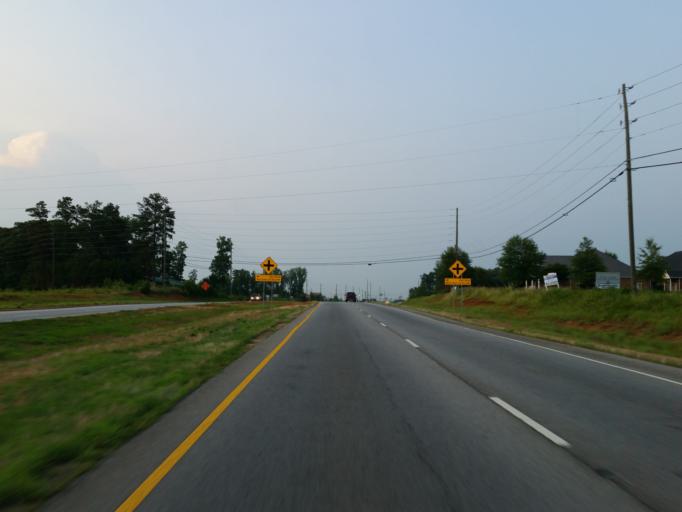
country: US
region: Georgia
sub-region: Henry County
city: McDonough
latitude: 33.4155
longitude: -84.1949
